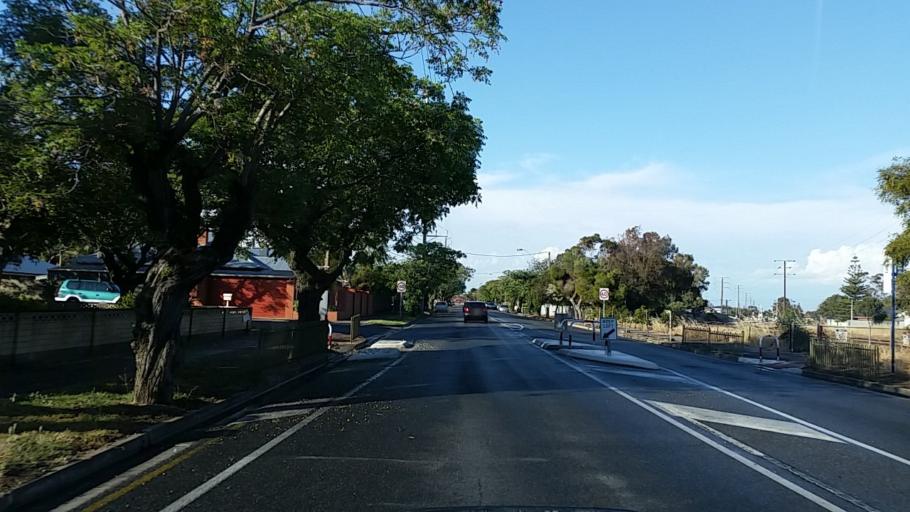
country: AU
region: South Australia
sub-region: Port Adelaide Enfield
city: Birkenhead
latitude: -34.8227
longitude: 138.4916
